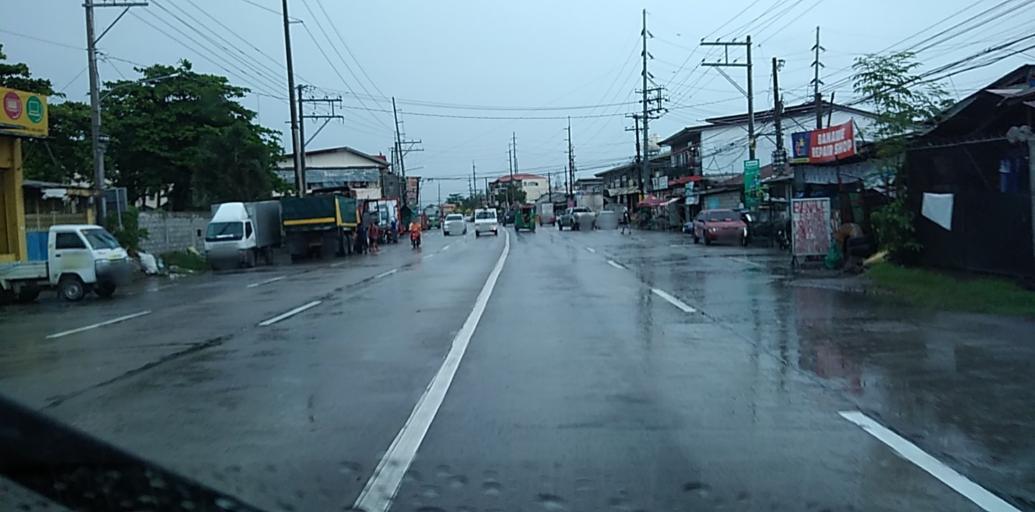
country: PH
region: Central Luzon
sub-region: Province of Pampanga
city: Mexico
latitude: 15.0528
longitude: 120.7089
